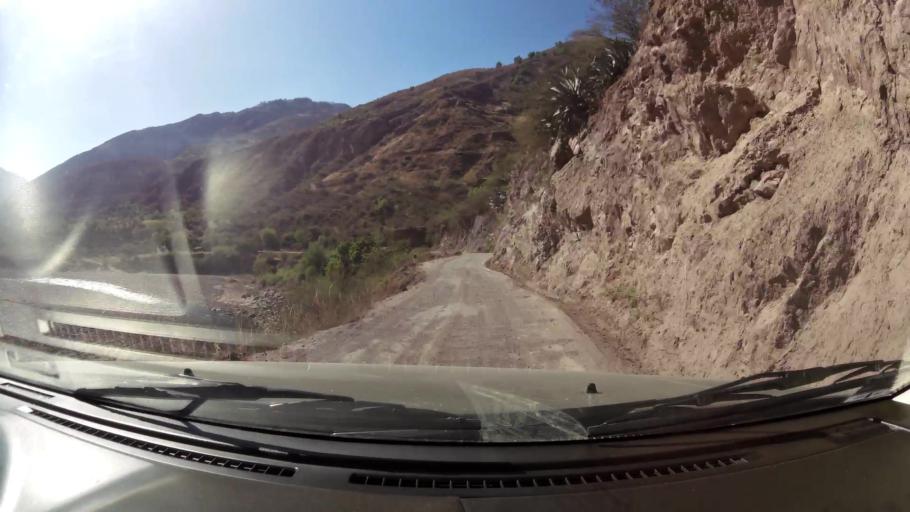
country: PE
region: Huancavelica
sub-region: Provincia de Acobamba
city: Pomacocha
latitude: -12.7723
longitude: -74.4985
